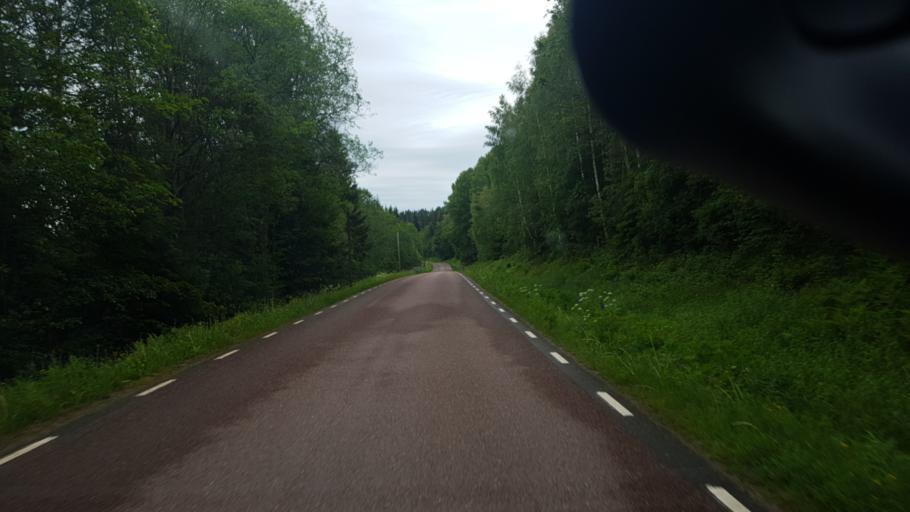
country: NO
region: Ostfold
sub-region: Romskog
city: Romskog
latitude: 59.7483
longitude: 12.0548
